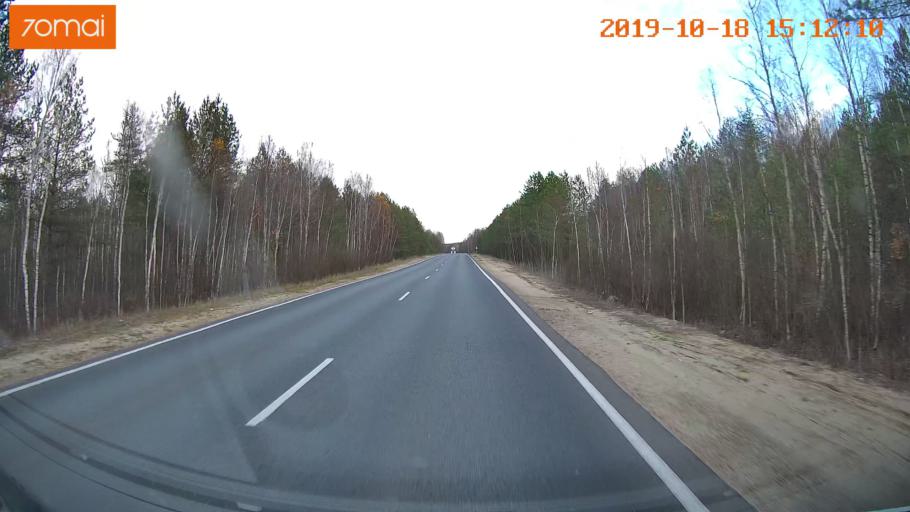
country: RU
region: Vladimir
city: Gus'-Khrustal'nyy
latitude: 55.5746
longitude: 40.6905
